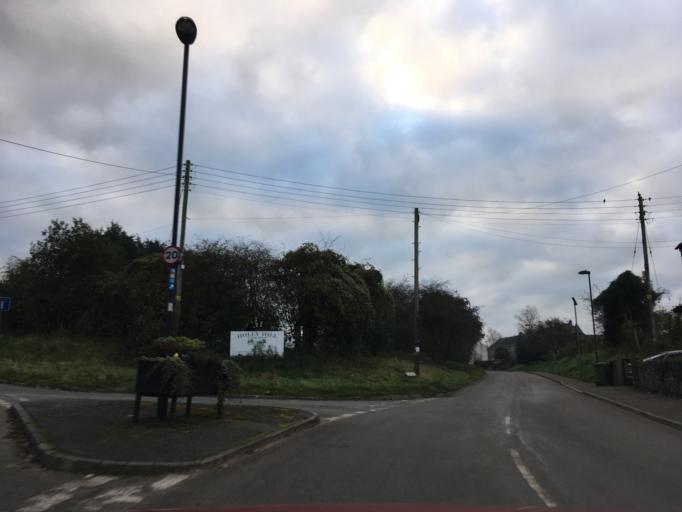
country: GB
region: England
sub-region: South Gloucestershire
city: Yate
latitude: 51.5491
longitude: -2.4603
